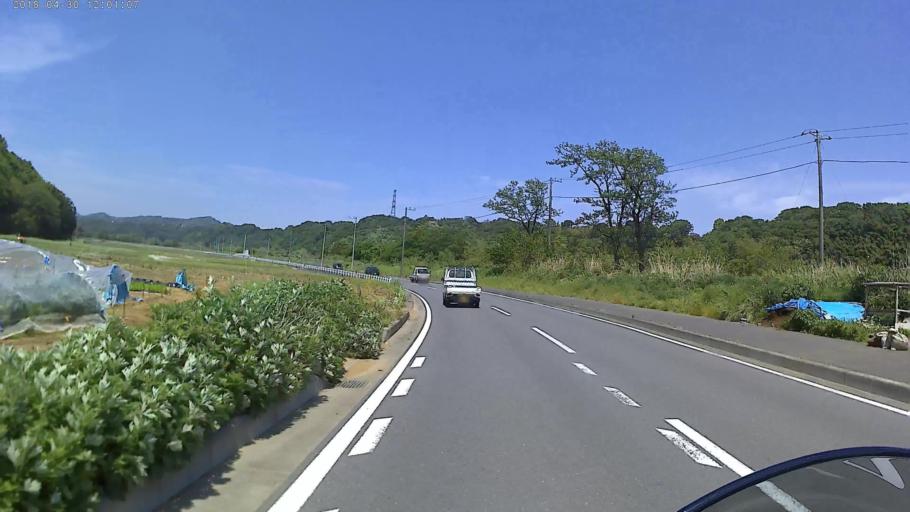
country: JP
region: Kanagawa
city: Zama
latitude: 35.5148
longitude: 139.3263
